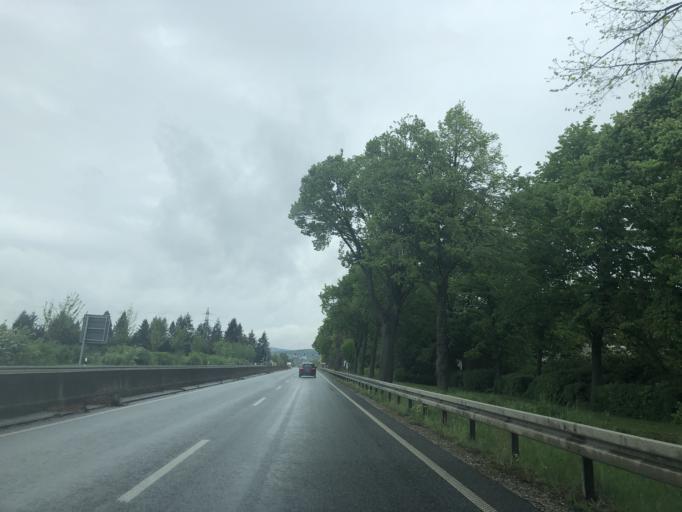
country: DE
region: Hesse
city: Sulzbach
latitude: 50.1300
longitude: 8.5168
